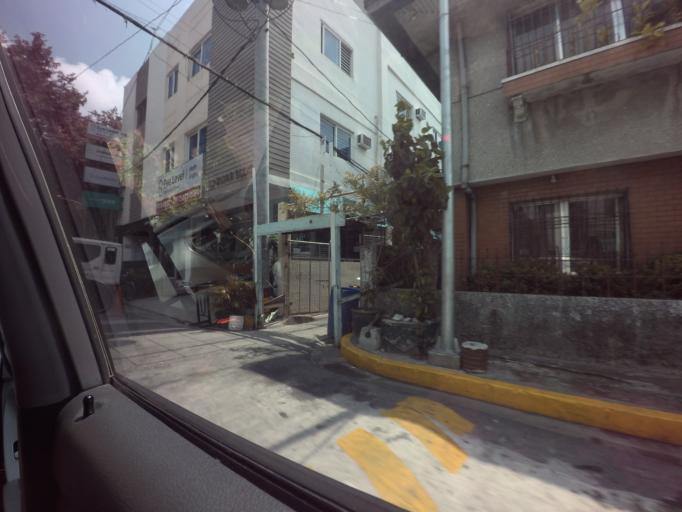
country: PH
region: Metro Manila
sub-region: City of Manila
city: Quiapo
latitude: 14.5906
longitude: 121.0030
